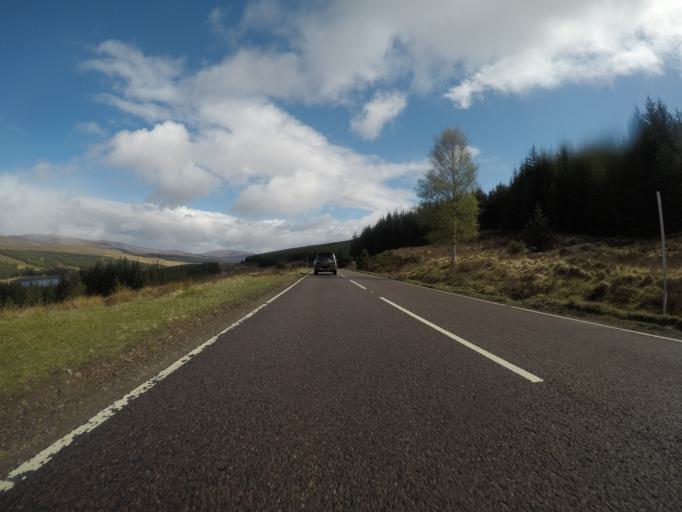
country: GB
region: Scotland
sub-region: Highland
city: Spean Bridge
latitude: 57.1034
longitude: -4.9882
